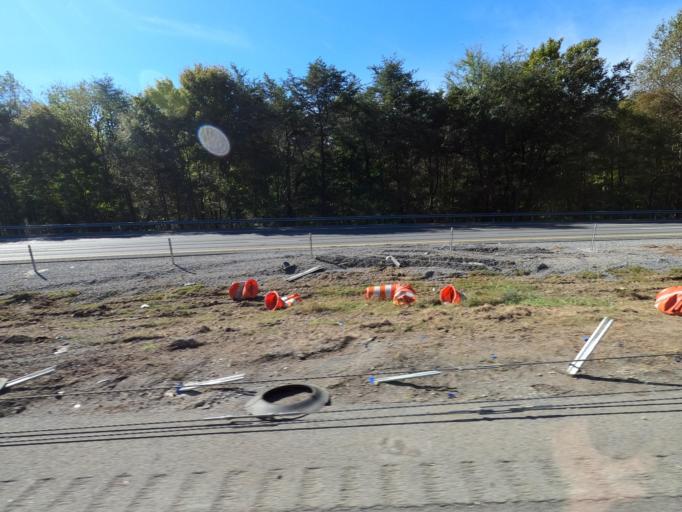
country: US
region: Tennessee
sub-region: Williamson County
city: Fairview
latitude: 36.0240
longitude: -87.1897
